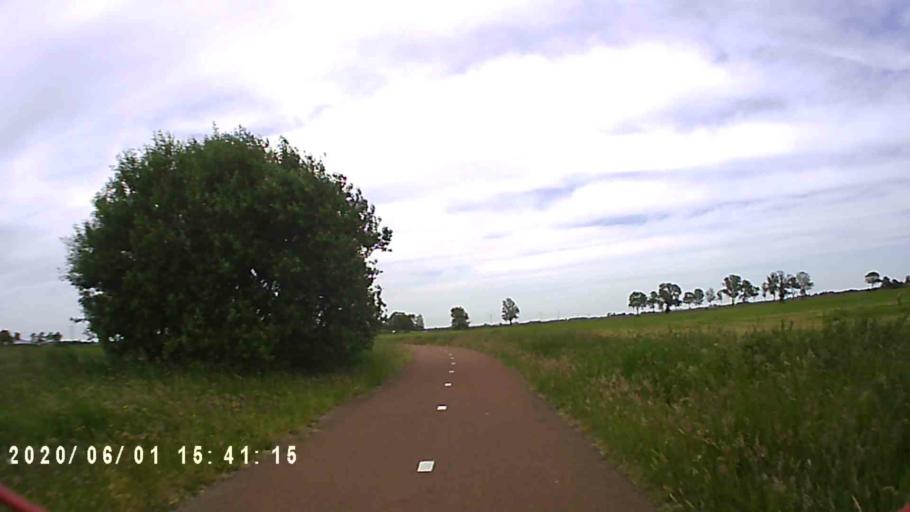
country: NL
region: Friesland
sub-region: Gemeente Boarnsterhim
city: Wergea
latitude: 53.1554
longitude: 5.8244
